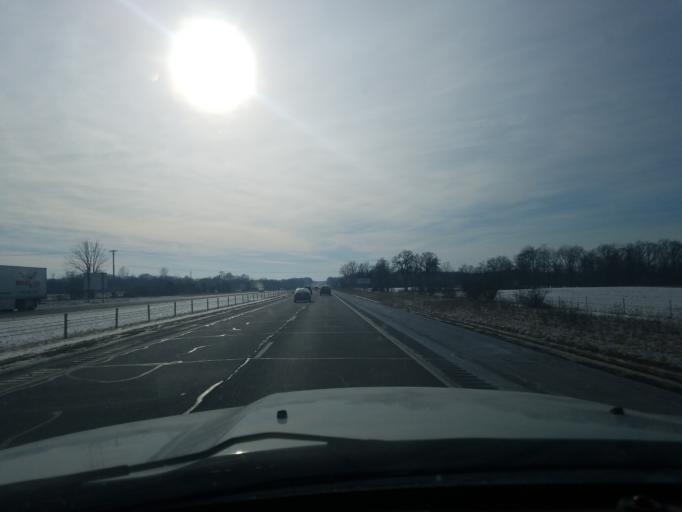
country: US
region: Indiana
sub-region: Huntington County
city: Warren
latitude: 40.7128
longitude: -85.4461
